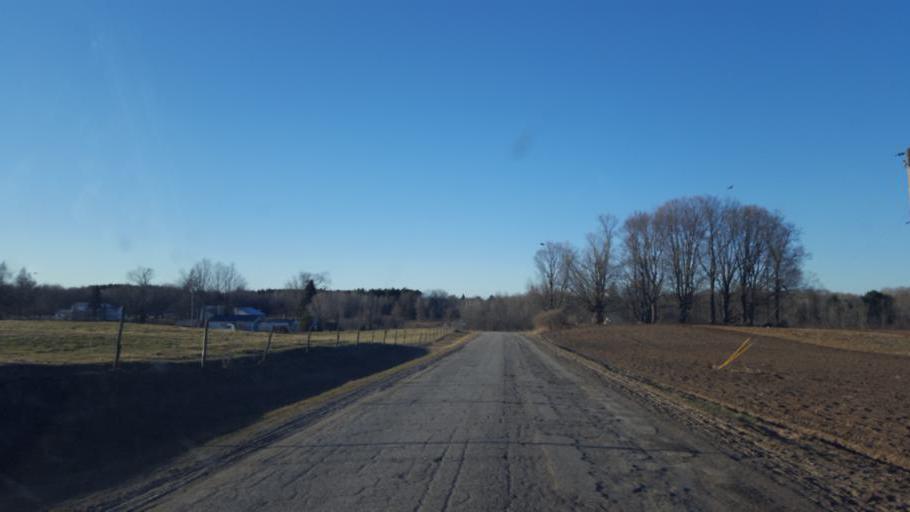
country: US
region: Michigan
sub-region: Mecosta County
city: Canadian Lakes
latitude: 43.5528
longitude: -85.3929
